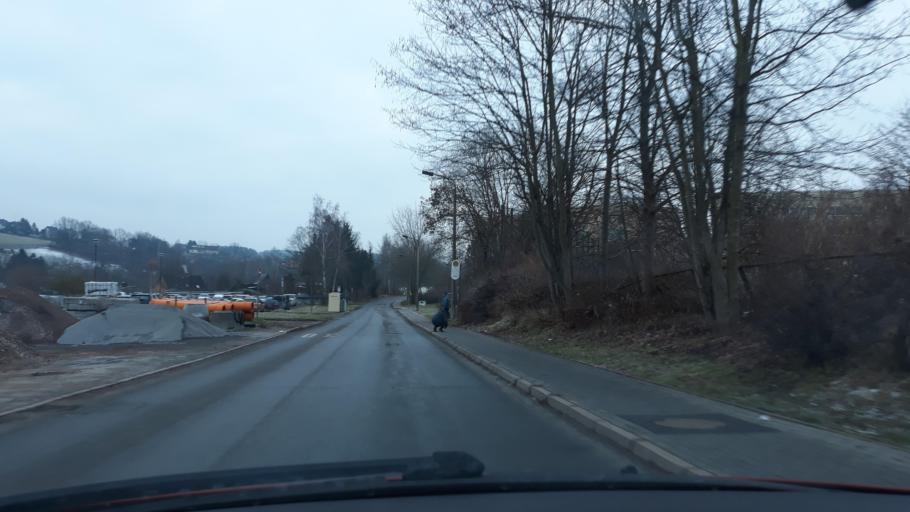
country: DE
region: Saxony
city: Kirchberg
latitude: 50.6197
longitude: 12.5169
